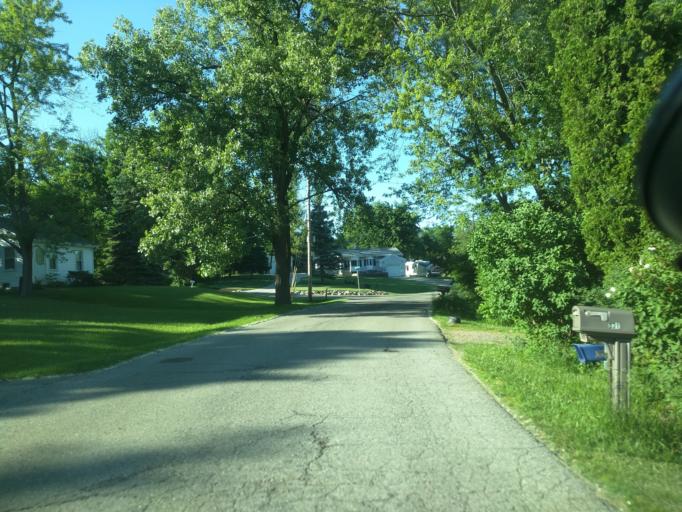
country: US
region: Michigan
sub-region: Ingham County
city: Edgemont Park
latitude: 42.7439
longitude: -84.5947
